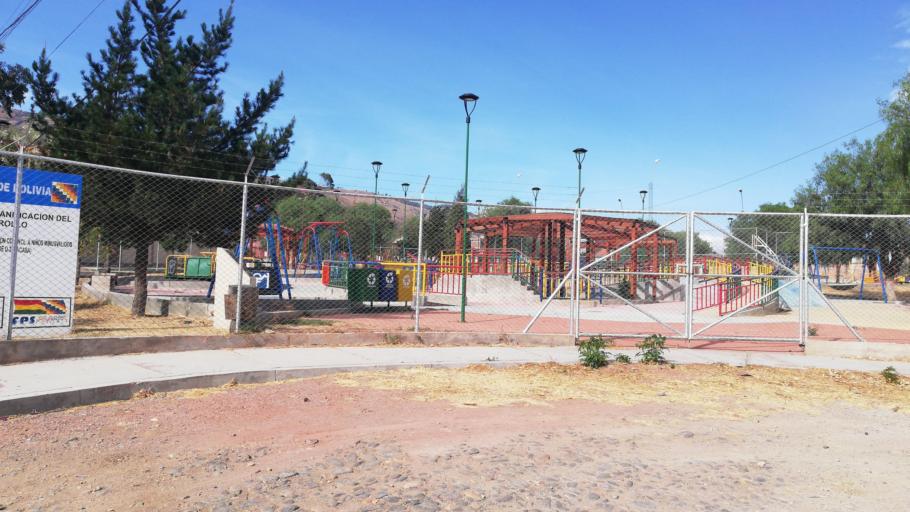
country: BO
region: Cochabamba
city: Cochabamba
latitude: -17.3801
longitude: -66.1003
